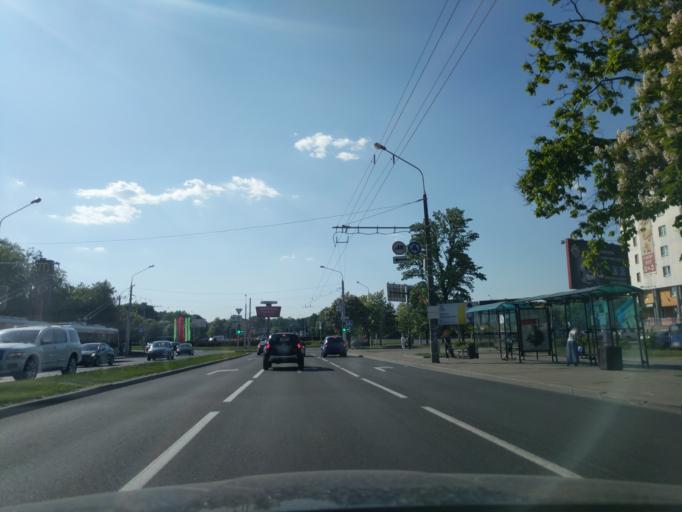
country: BY
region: Minsk
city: Minsk
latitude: 53.9307
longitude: 27.5791
